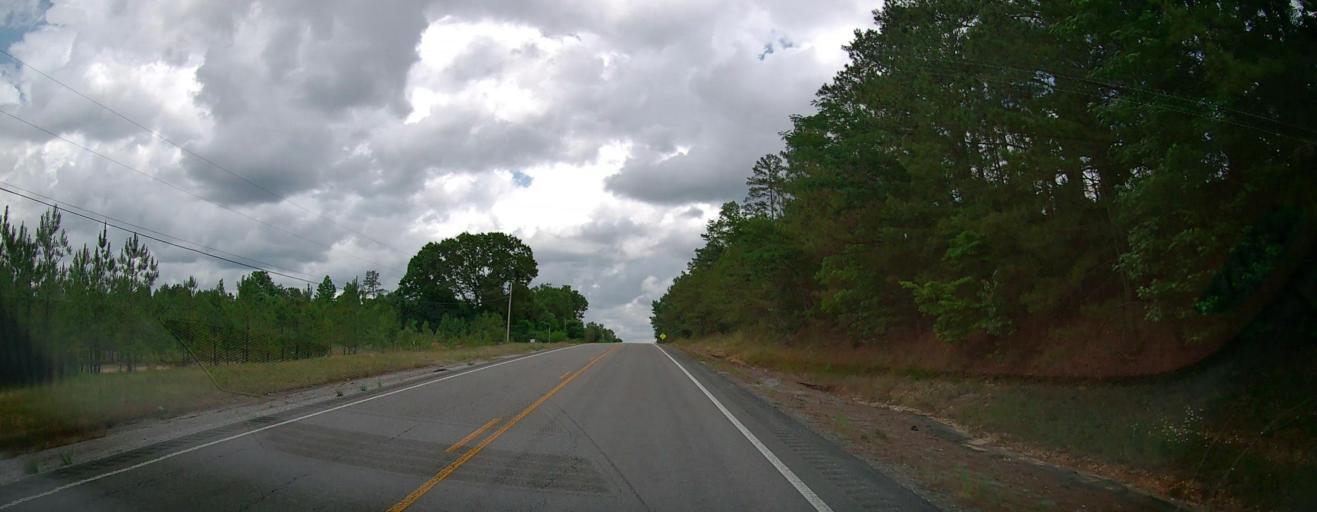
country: US
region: Alabama
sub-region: Marion County
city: Hamilton
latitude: 34.1323
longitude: -88.0241
